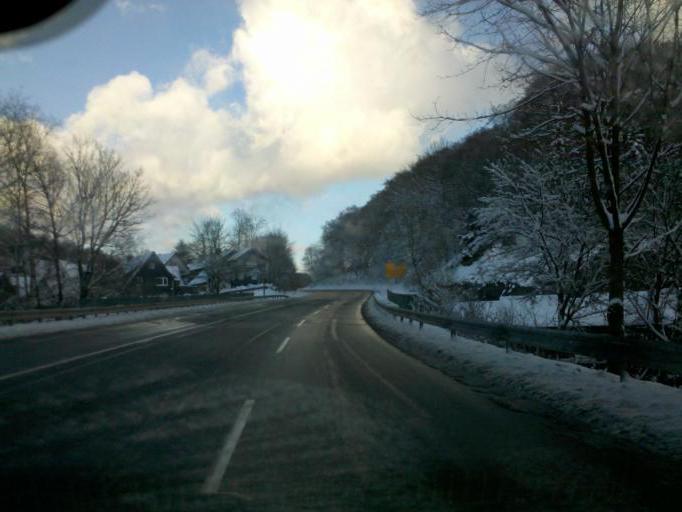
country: DE
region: North Rhine-Westphalia
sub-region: Regierungsbezirk Arnsberg
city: Drolshagen
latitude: 51.0440
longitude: 7.7425
